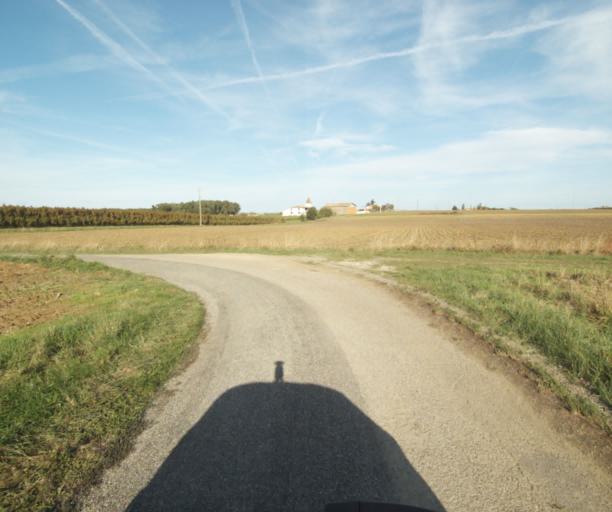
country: FR
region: Midi-Pyrenees
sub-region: Departement du Tarn-et-Garonne
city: Finhan
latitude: 43.9196
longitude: 1.1268
